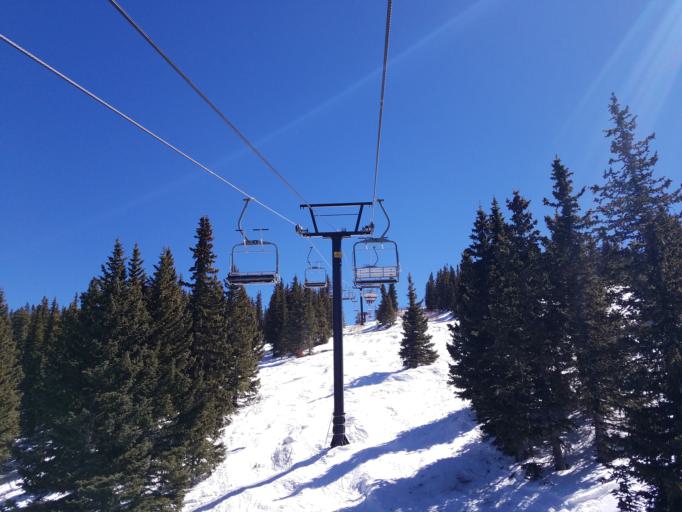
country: US
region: New Mexico
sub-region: Santa Fe County
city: Santa Fe
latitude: 35.7881
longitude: -105.7837
